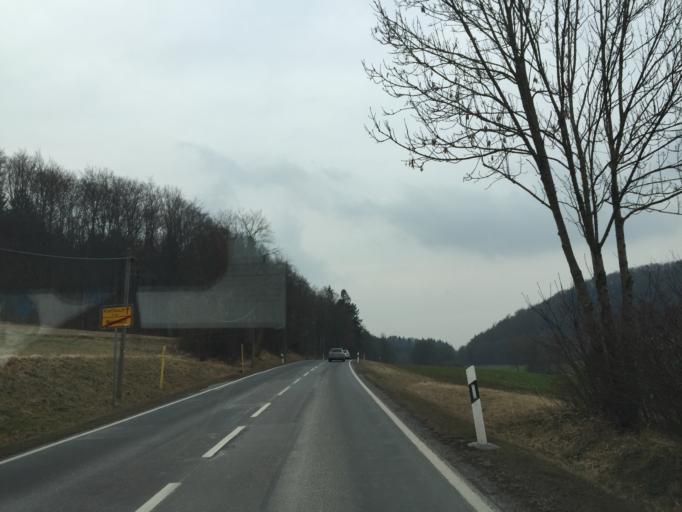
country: DE
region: Thuringia
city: Nauendorf
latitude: 50.8953
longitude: 11.1766
